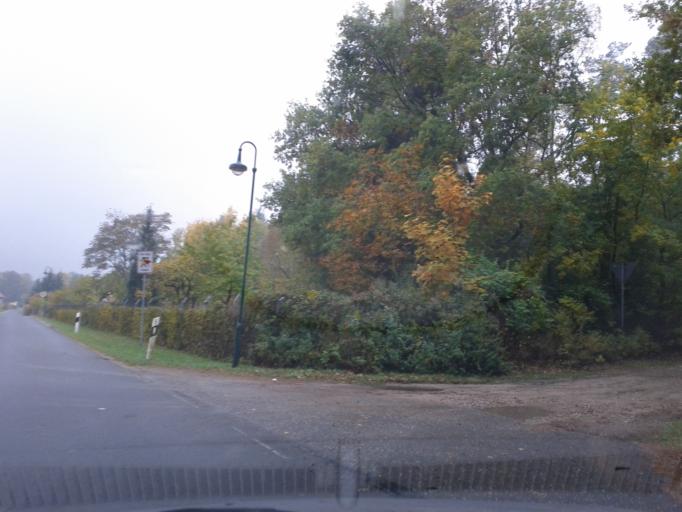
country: DE
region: Brandenburg
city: Spreenhagen
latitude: 52.3840
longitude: 13.8745
